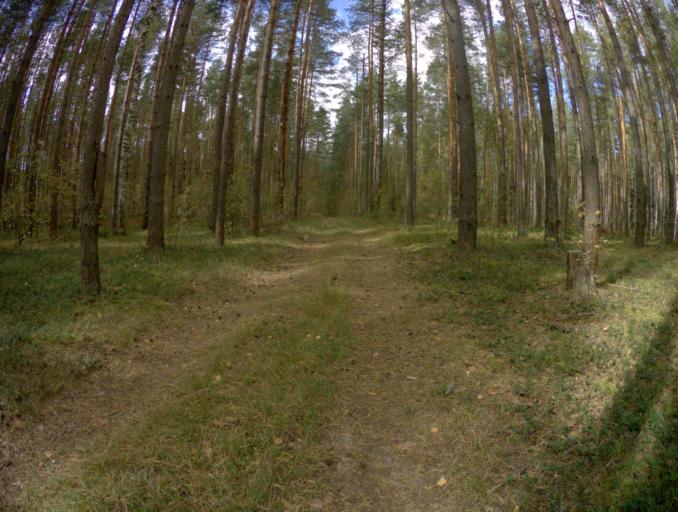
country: RU
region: Moskovskaya
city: Kerva
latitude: 55.7187
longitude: 39.5808
